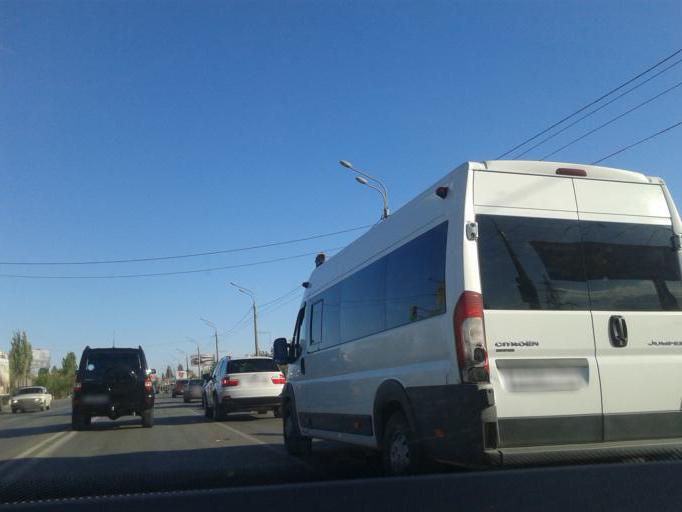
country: RU
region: Volgograd
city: Gorodishche
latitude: 48.7655
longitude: 44.4746
